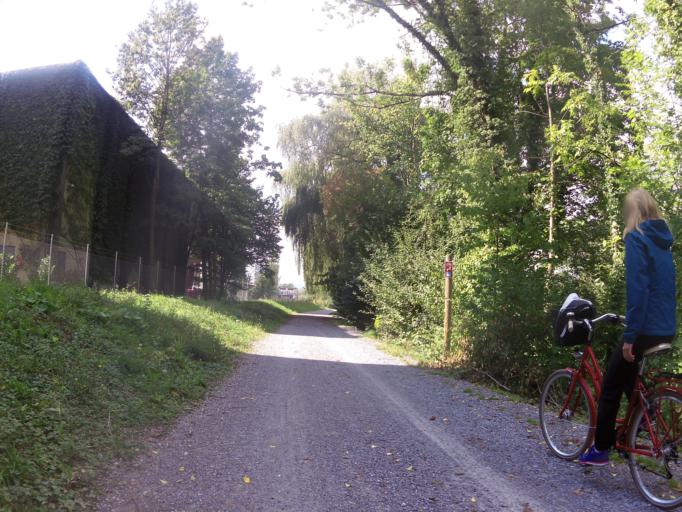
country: CH
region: Zurich
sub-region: Bezirk Zuerich
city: Zuerich (Kreis 10) / Hoengg
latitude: 47.3983
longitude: 8.4905
